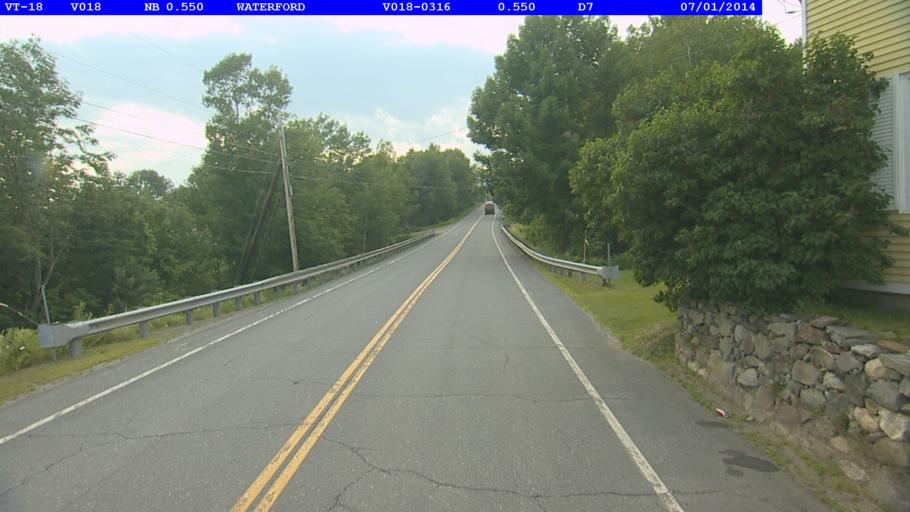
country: US
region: New Hampshire
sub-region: Grafton County
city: Littleton
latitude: 44.3491
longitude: -71.8953
